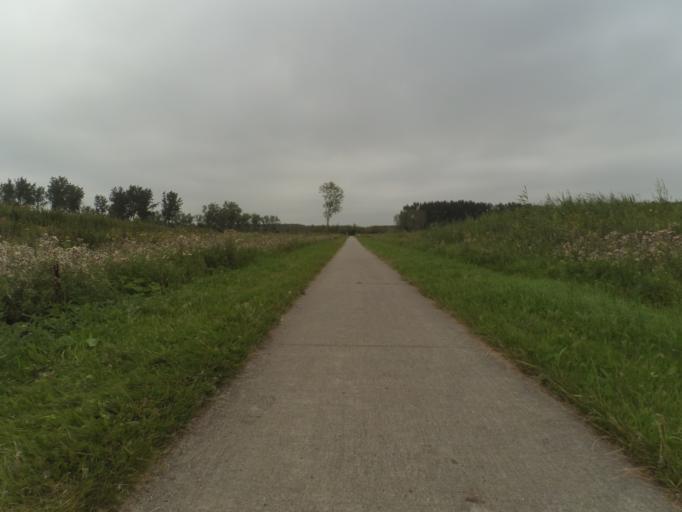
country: NL
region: Flevoland
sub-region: Gemeente Almere
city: Almere Stad
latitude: 52.4088
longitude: 5.3413
